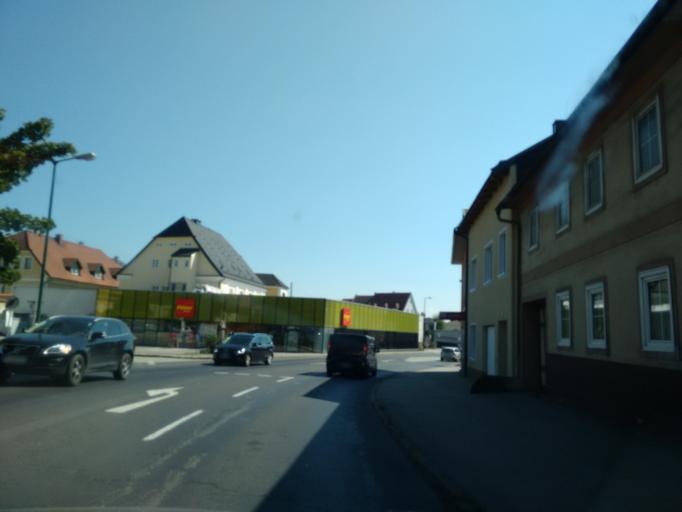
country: AT
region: Upper Austria
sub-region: Politischer Bezirk Urfahr-Umgebung
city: Feldkirchen an der Donau
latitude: 48.3094
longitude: 14.0204
